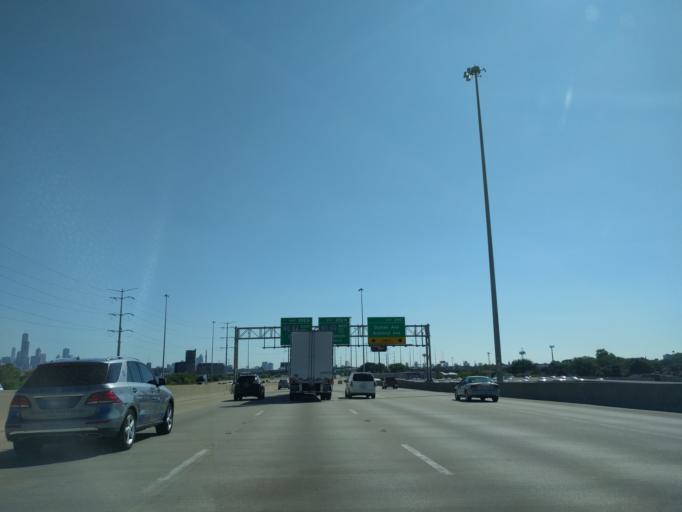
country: US
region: Illinois
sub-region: Cook County
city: Chicago
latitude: 41.8353
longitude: -87.6848
